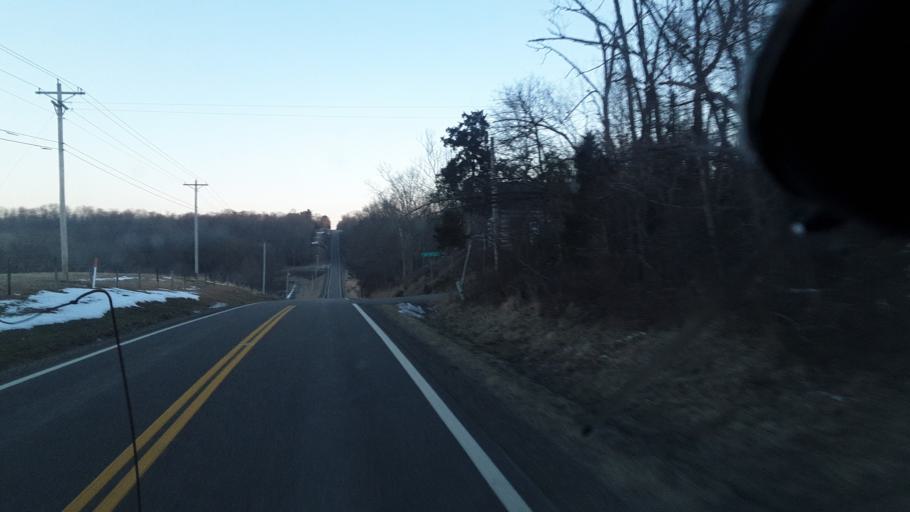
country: US
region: Ohio
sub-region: Perry County
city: Somerset
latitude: 39.7624
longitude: -82.3039
